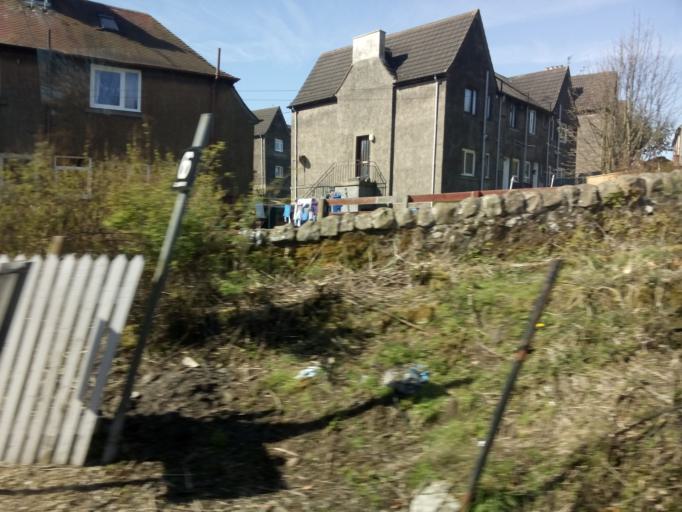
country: GB
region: Scotland
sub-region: Fife
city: North Queensferry
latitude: 56.0130
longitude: -3.3950
